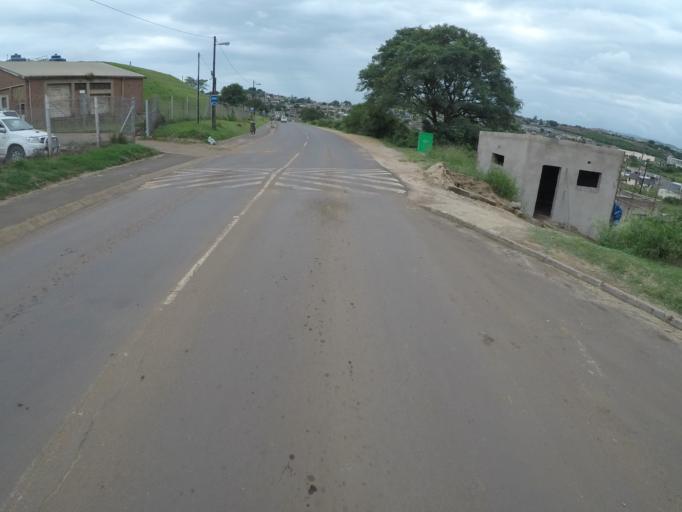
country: ZA
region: KwaZulu-Natal
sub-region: uThungulu District Municipality
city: Empangeni
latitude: -28.7784
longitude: 31.8641
